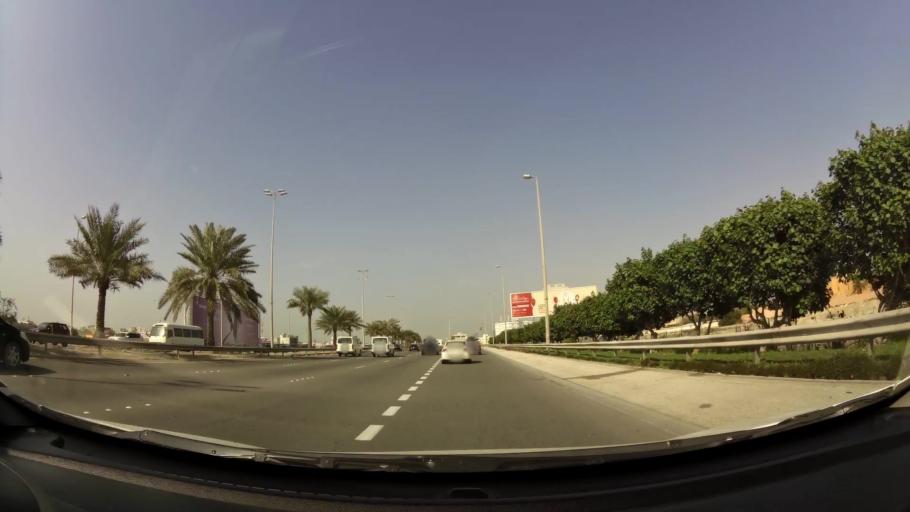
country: BH
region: Manama
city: Jidd Hafs
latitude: 26.2116
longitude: 50.5190
